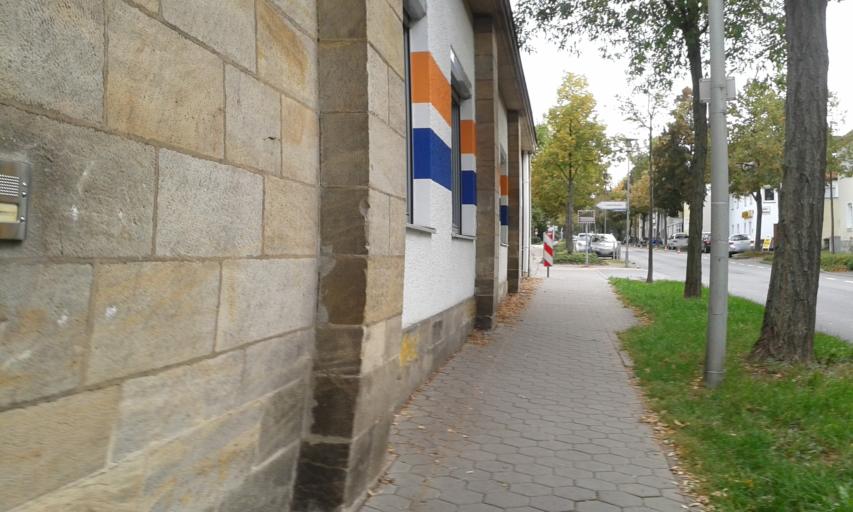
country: DE
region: Bavaria
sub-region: Upper Franconia
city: Bayreuth
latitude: 49.9502
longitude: 11.5822
